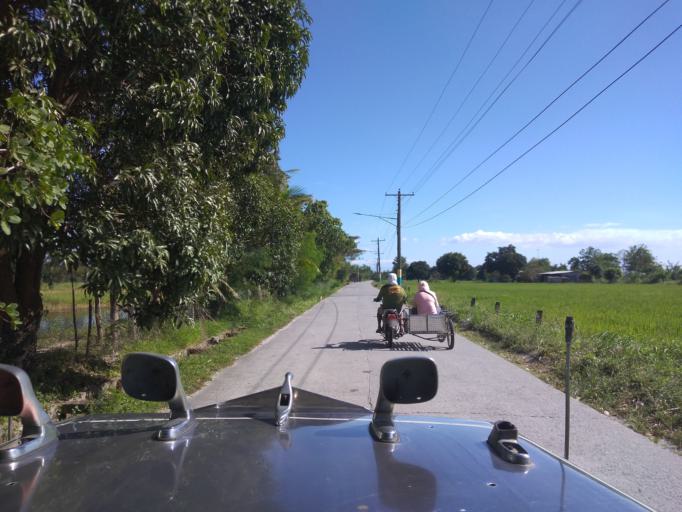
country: PH
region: Central Luzon
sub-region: Province of Pampanga
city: Bacolor
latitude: 15.0221
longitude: 120.6384
